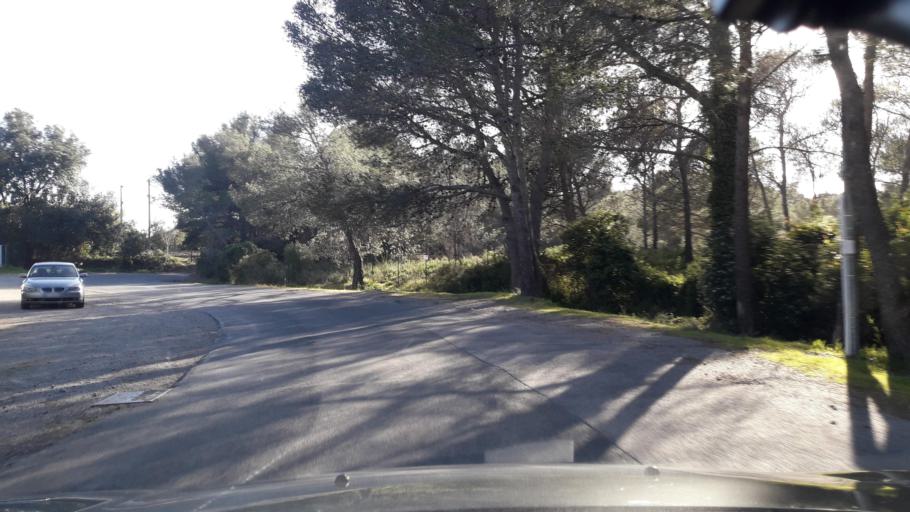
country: FR
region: Provence-Alpes-Cote d'Azur
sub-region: Departement du Var
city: Saint-Raphael
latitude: 43.4195
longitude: 6.8225
